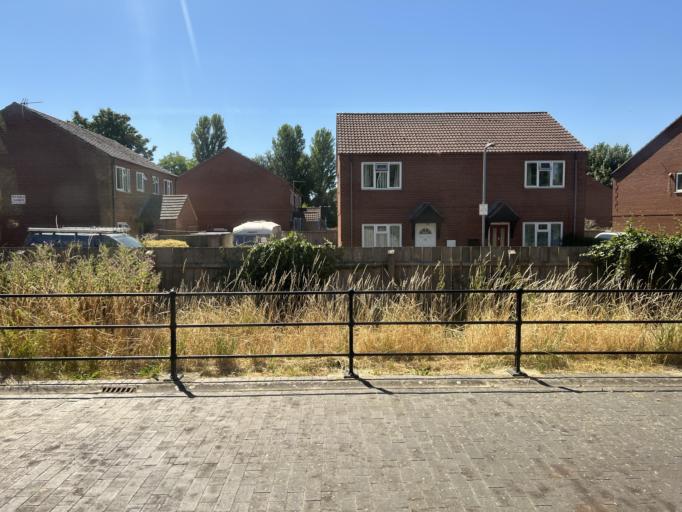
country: GB
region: England
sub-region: Lincolnshire
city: Wainfleet All Saints
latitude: 53.1054
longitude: 0.2338
